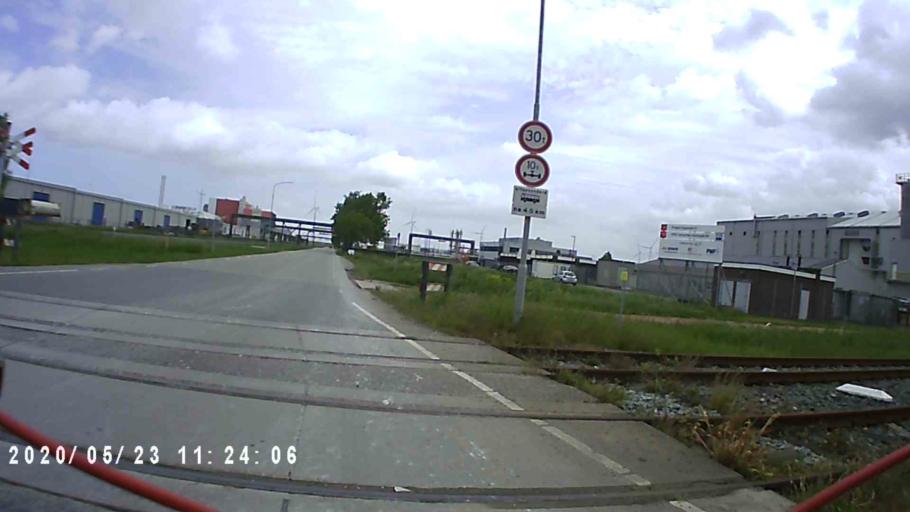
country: NL
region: Groningen
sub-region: Gemeente Delfzijl
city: Delfzijl
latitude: 53.3025
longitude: 6.9860
